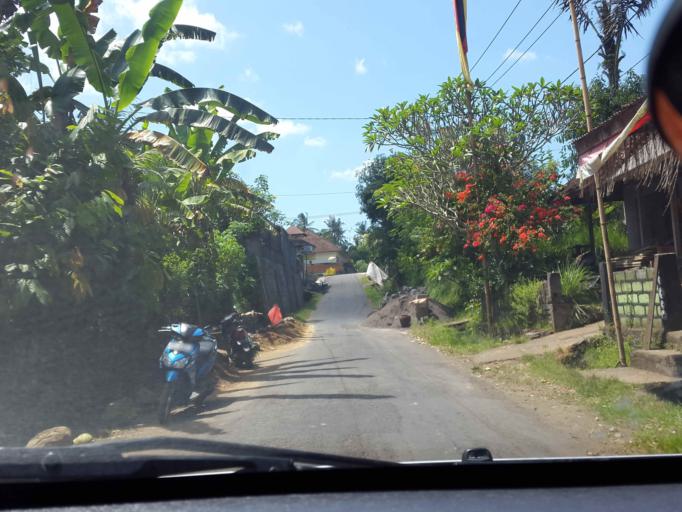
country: ID
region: Bali
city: Banjar Wangsian
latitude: -8.4989
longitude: 115.3973
